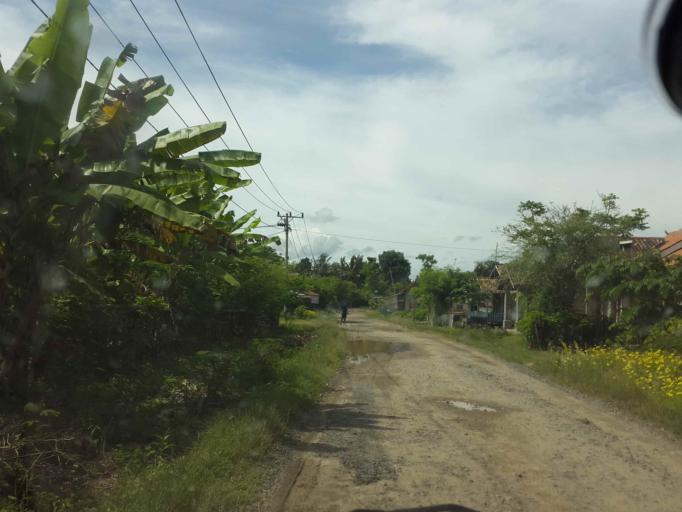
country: ID
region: Lampung
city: Sidorejo
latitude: -5.6418
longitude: 105.4522
